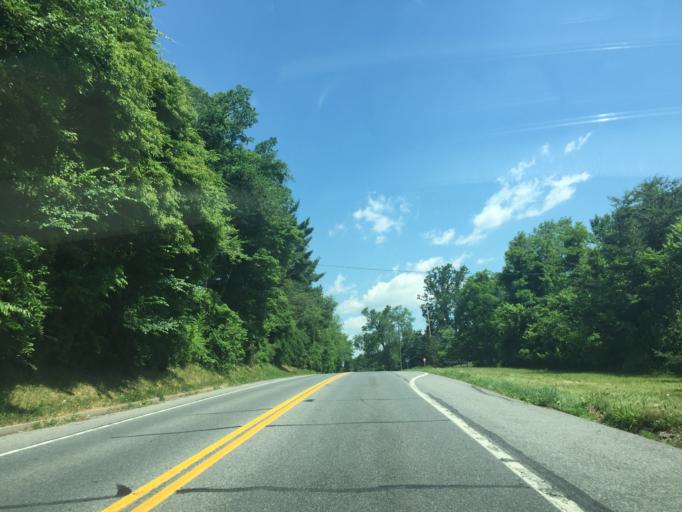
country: US
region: Maryland
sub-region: Baltimore County
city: Reisterstown
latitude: 39.4923
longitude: -76.8306
